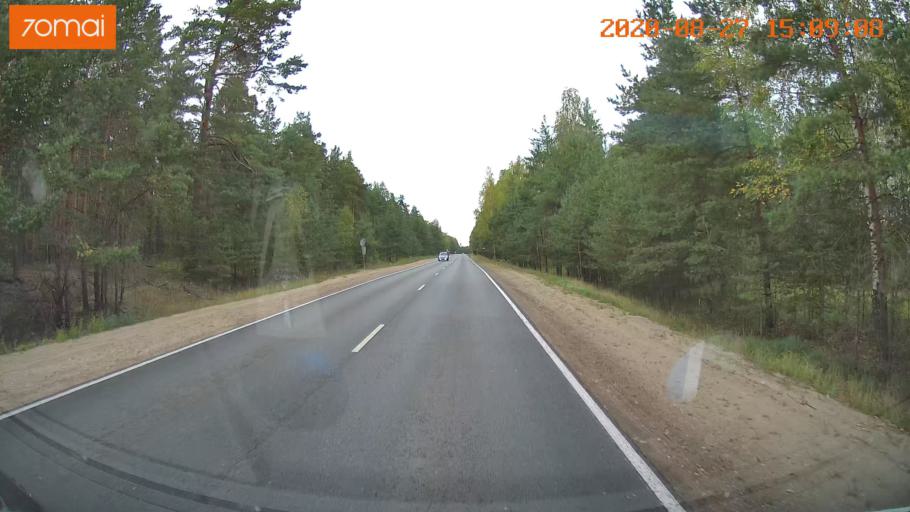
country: RU
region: Vladimir
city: Kurlovo
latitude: 55.5012
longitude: 40.5728
